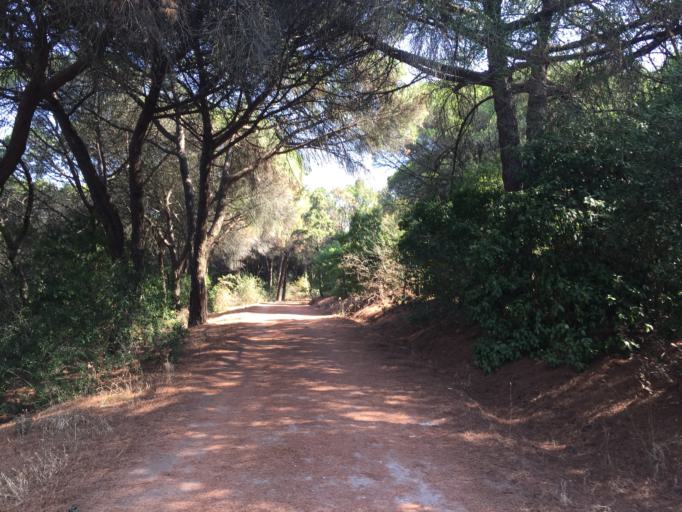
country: PT
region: Lisbon
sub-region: Oeiras
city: Alges
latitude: 38.7196
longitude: -9.2043
